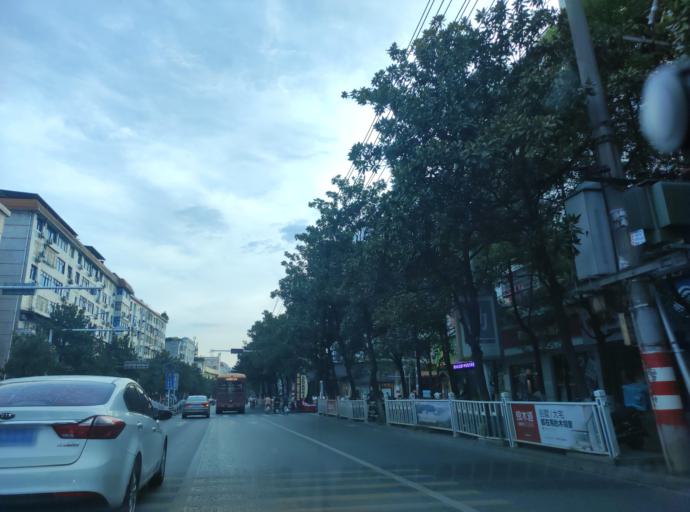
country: CN
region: Jiangxi Sheng
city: Pingxiang
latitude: 27.6334
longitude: 113.8551
